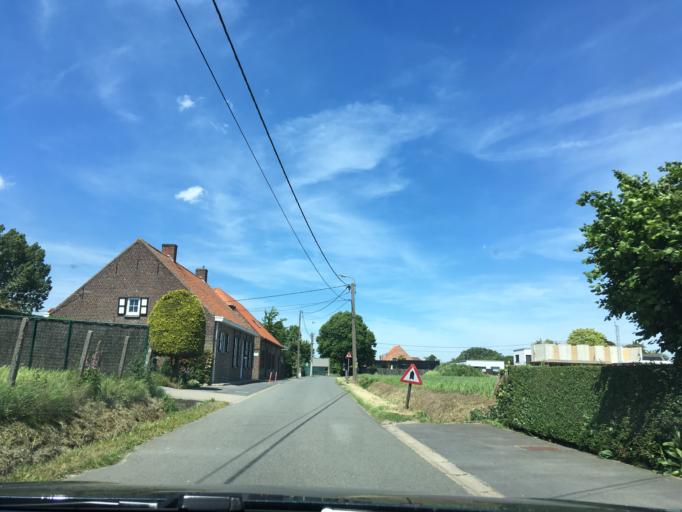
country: BE
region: Flanders
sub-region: Provincie West-Vlaanderen
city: Hooglede
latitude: 51.0058
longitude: 3.0963
